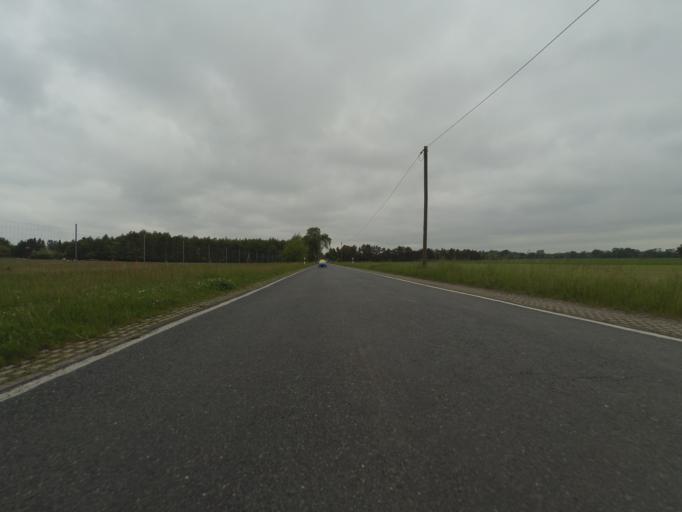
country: DE
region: Lower Saxony
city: Edemissen
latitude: 52.4466
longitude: 10.2717
